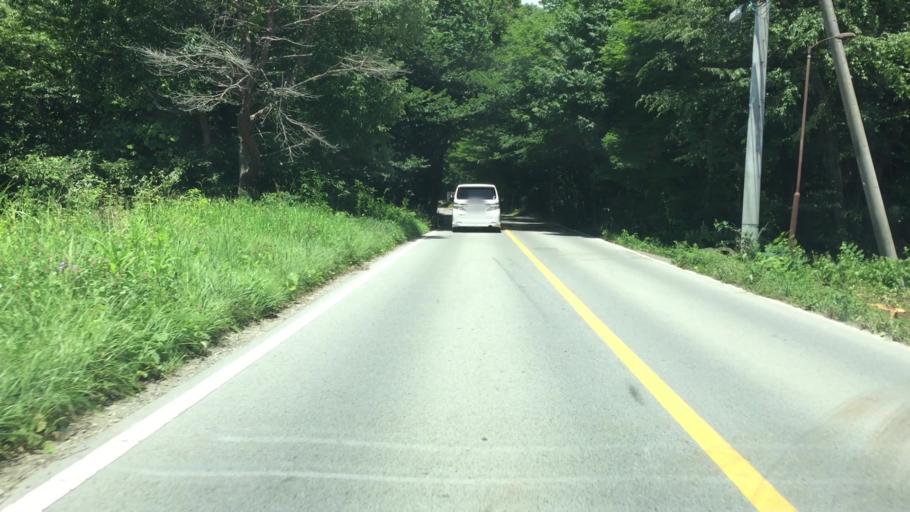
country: JP
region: Tochigi
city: Kuroiso
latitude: 37.0202
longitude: 140.0101
